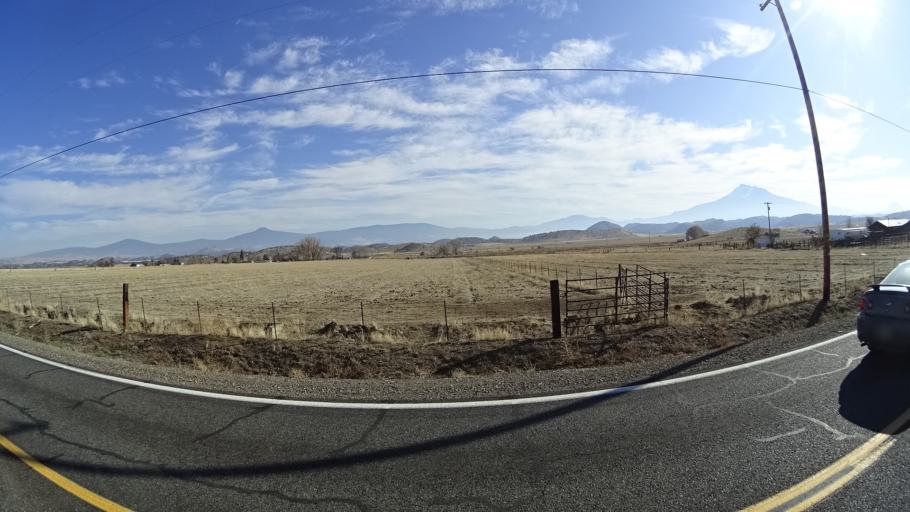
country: US
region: California
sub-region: Siskiyou County
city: Montague
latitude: 41.6166
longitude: -122.5300
